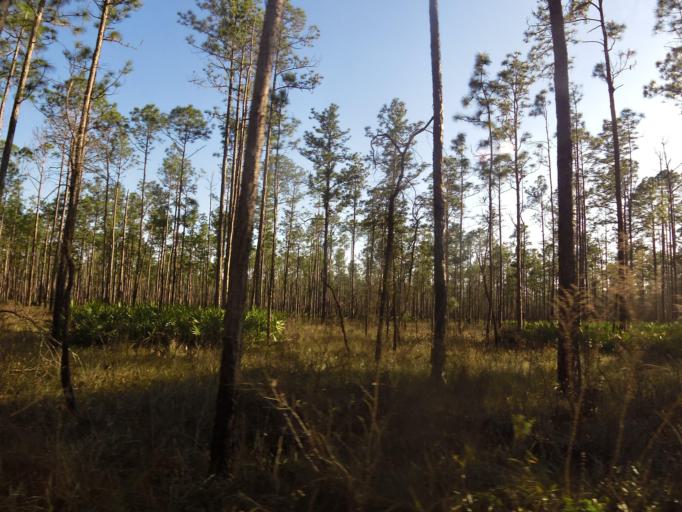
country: US
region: Florida
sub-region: Clay County
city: Middleburg
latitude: 30.1477
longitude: -81.9046
